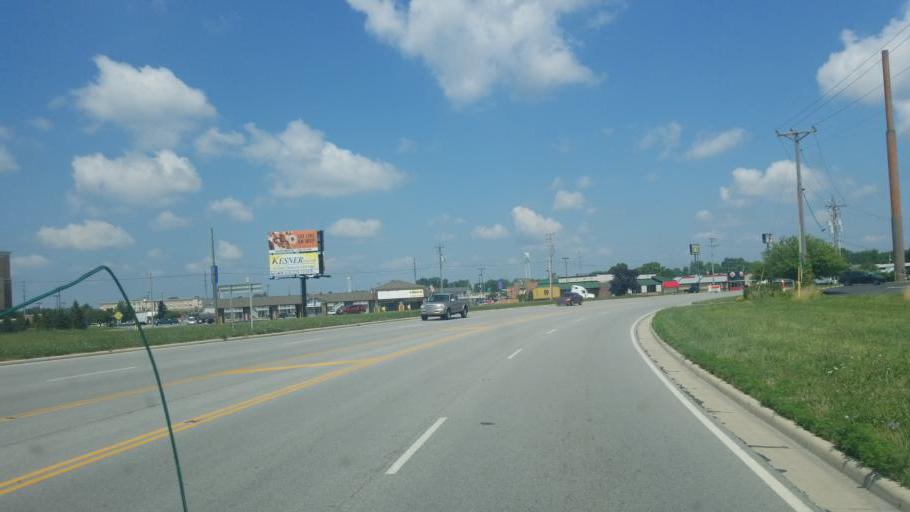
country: US
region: Ohio
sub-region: Allen County
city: Lima
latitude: 40.7282
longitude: -84.0698
